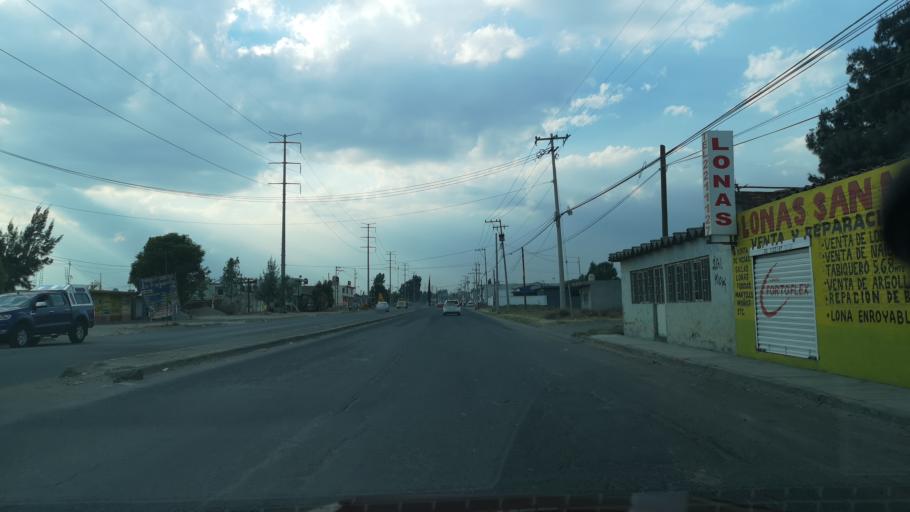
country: MX
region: Puebla
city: Cuanala
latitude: 19.0894
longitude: -98.3351
